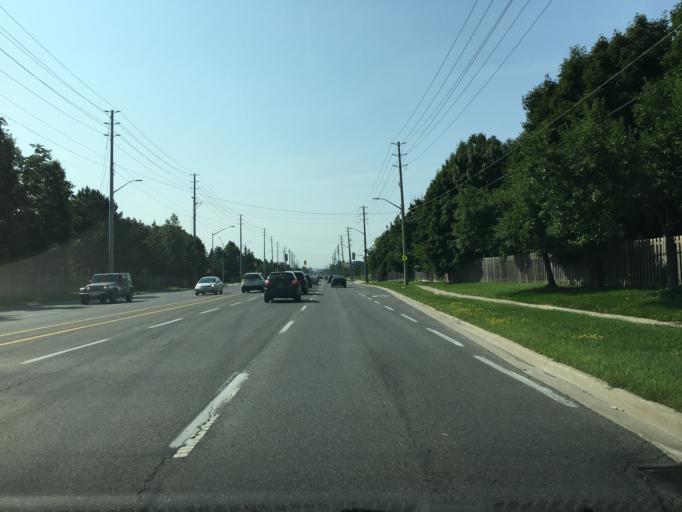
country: CA
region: Ontario
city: Markham
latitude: 43.8613
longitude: -79.3354
